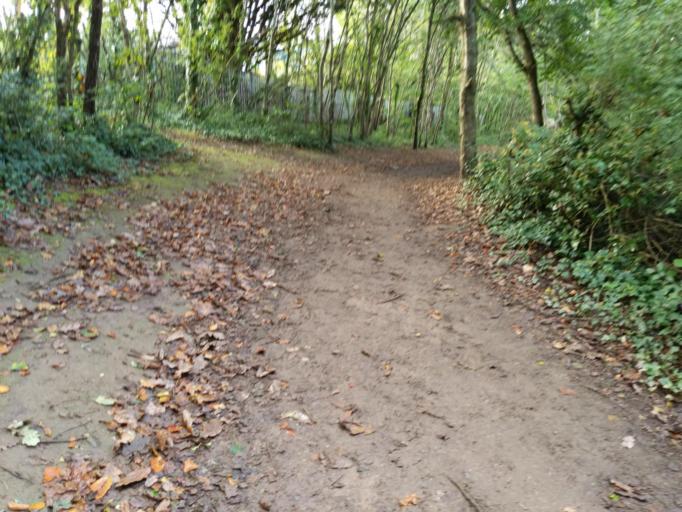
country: GB
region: England
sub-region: Cornwall
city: Saltash
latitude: 50.4238
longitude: -4.1881
